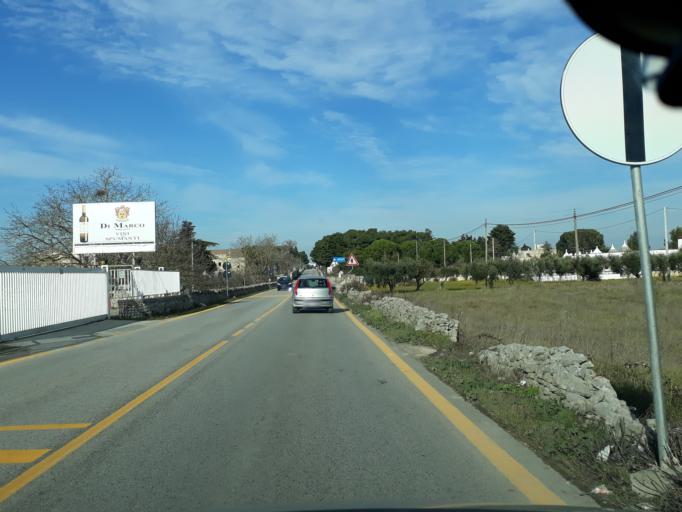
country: IT
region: Apulia
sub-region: Provincia di Taranto
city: Martina Franca
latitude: 40.7184
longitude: 17.3328
